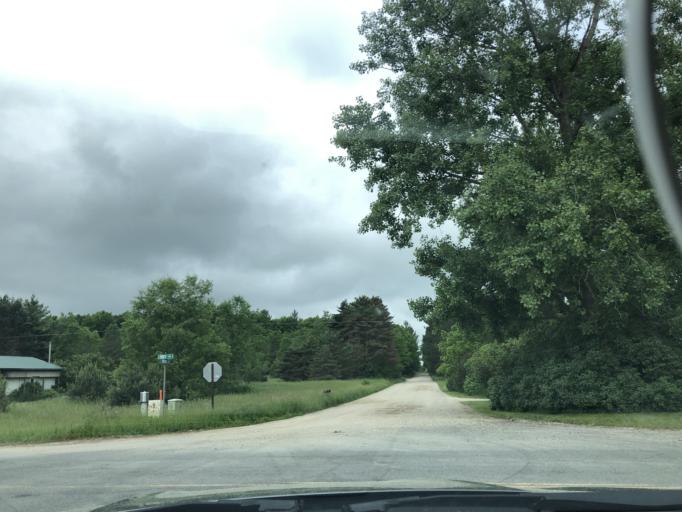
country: US
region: Michigan
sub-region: Missaukee County
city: Lake City
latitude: 44.4539
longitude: -85.2158
